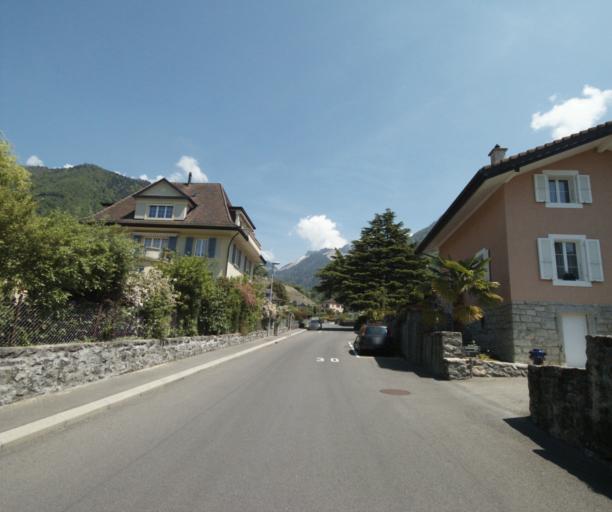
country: CH
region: Vaud
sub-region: Aigle District
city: Villeneuve
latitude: 46.4010
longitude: 6.9285
